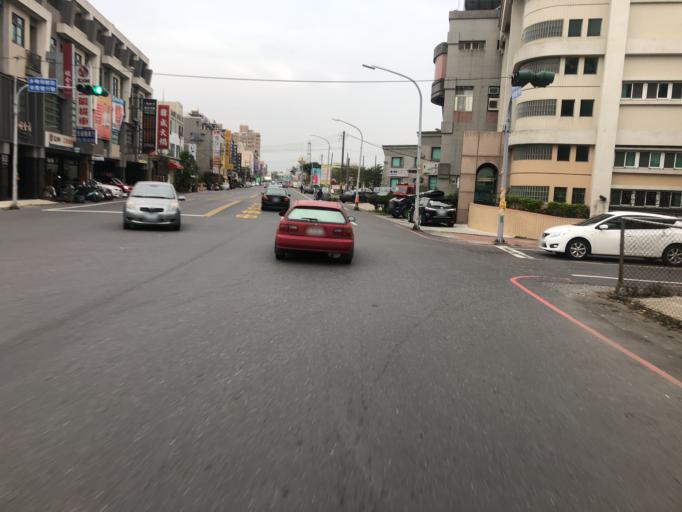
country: TW
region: Taiwan
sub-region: Tainan
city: Tainan
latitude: 23.1273
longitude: 120.2885
